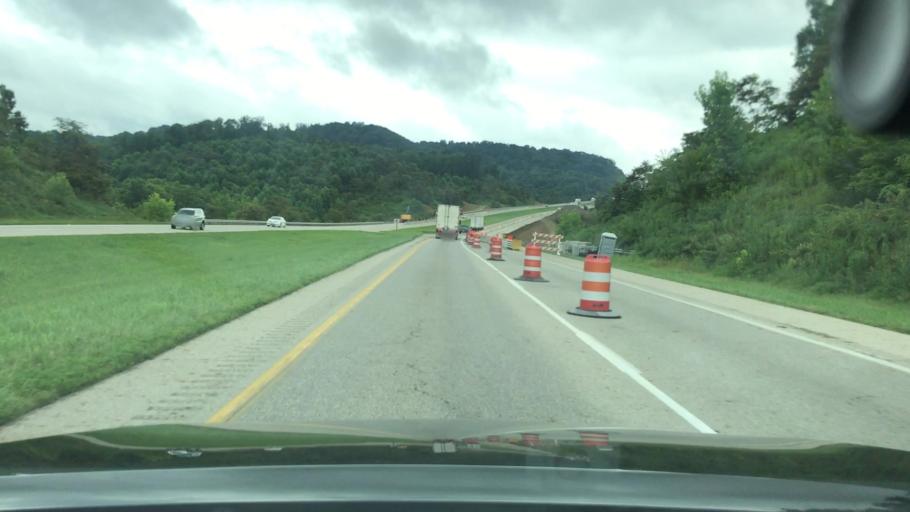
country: US
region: Ohio
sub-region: Ross County
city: Chillicothe
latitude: 39.2429
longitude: -82.8431
